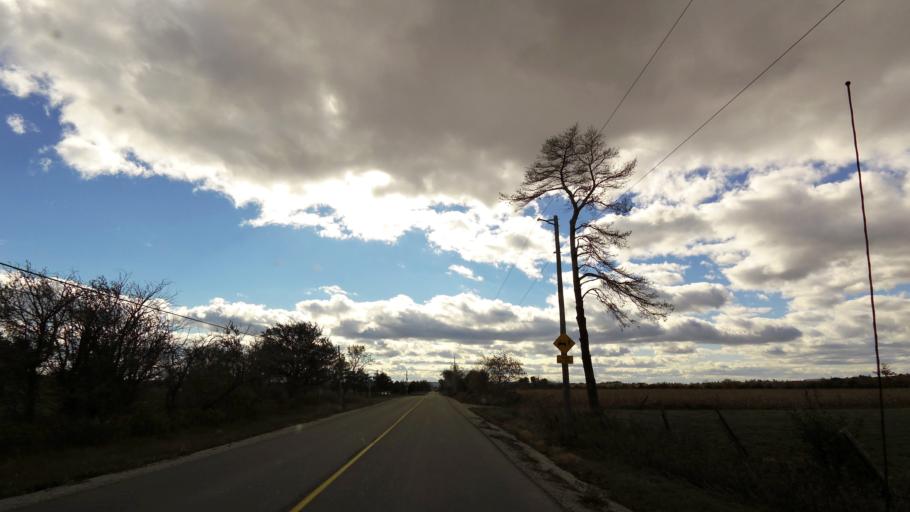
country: CA
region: Ontario
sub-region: Halton
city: Milton
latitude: 43.4860
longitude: -79.7872
